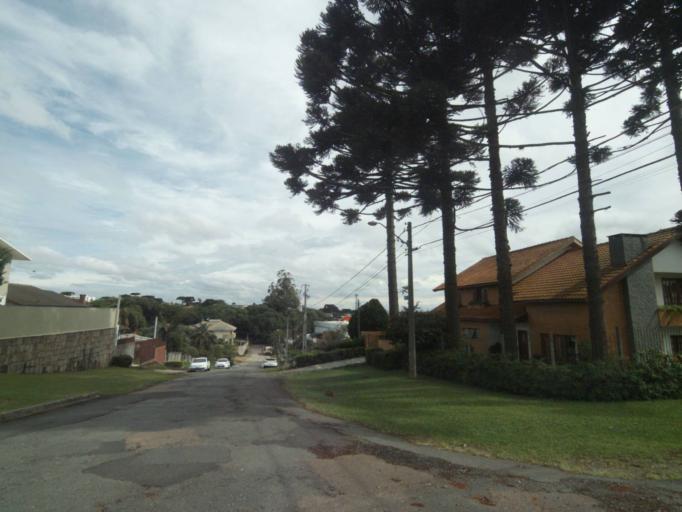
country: BR
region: Parana
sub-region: Curitiba
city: Curitiba
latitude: -25.4402
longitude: -49.3054
